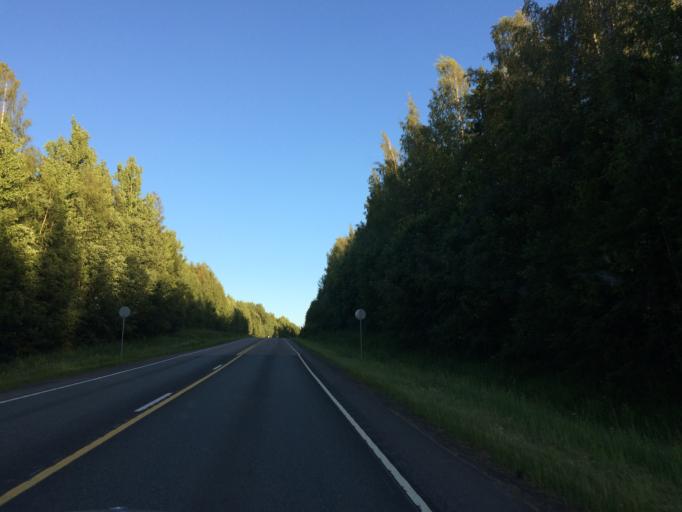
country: FI
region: Haeme
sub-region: Riihimaeki
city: Riihimaeki
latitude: 60.7652
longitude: 24.7111
